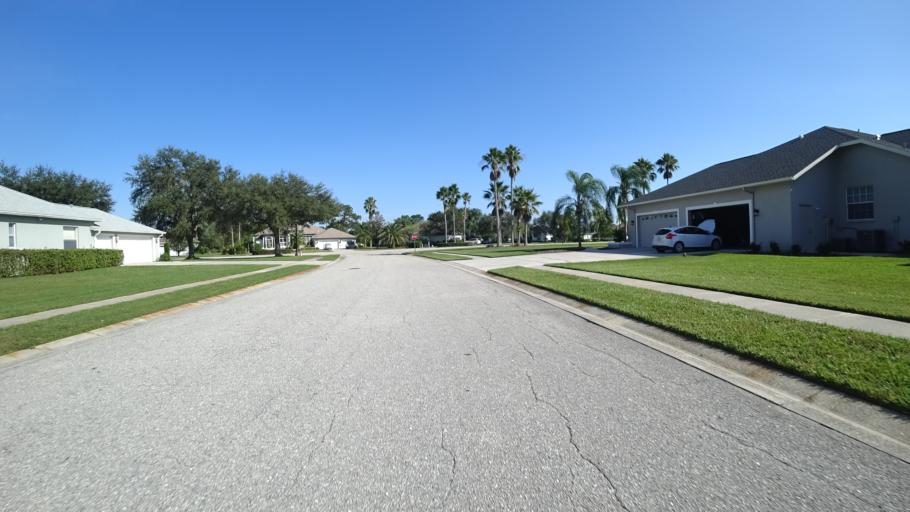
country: US
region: Florida
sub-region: Sarasota County
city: The Meadows
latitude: 27.4149
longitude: -82.4376
